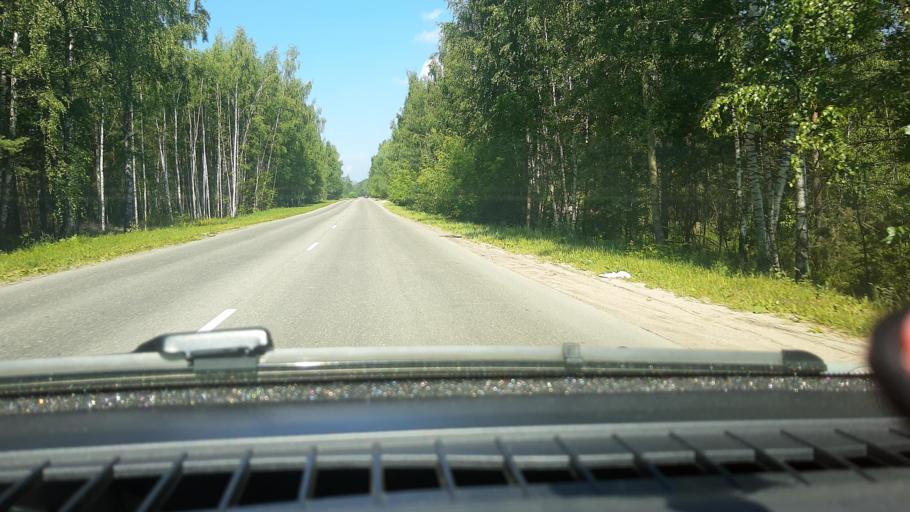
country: RU
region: Nizjnij Novgorod
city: Afonino
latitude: 56.3105
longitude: 44.1713
